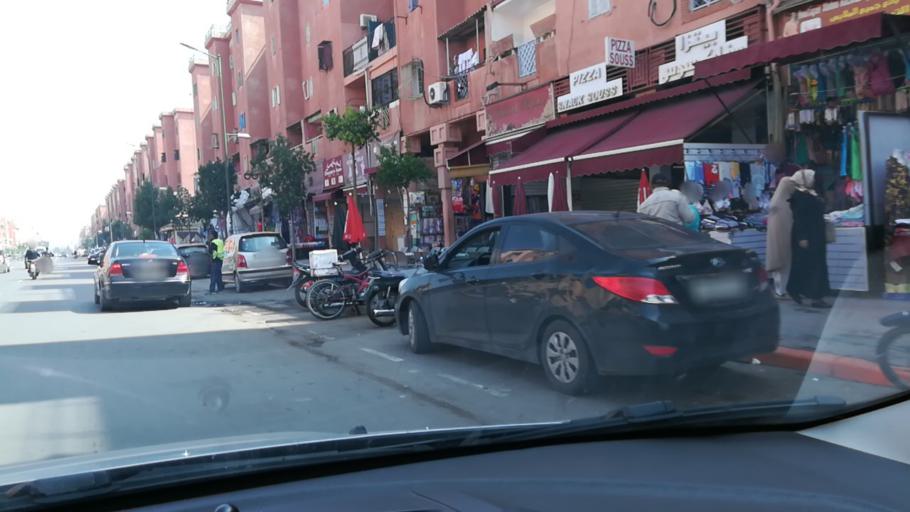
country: MA
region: Marrakech-Tensift-Al Haouz
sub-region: Marrakech
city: Marrakesh
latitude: 31.6295
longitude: -8.0583
